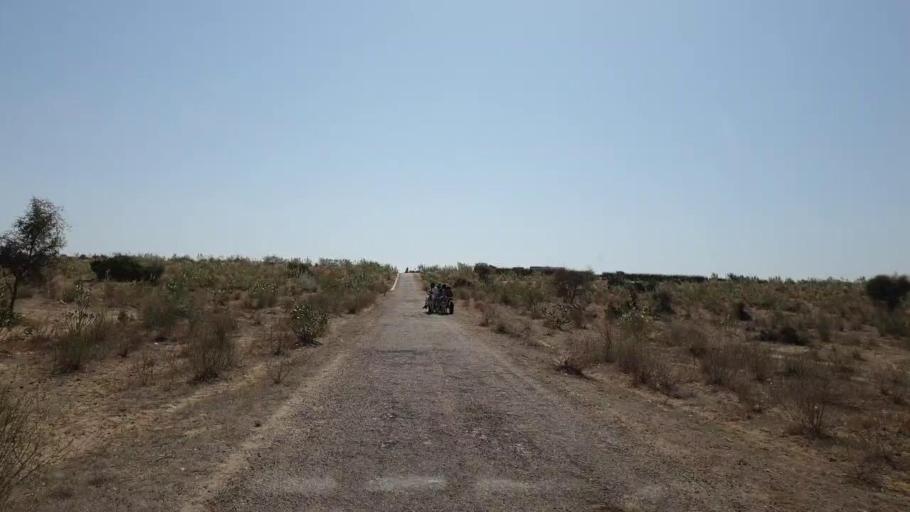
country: PK
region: Sindh
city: Nabisar
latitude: 25.0784
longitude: 69.9815
